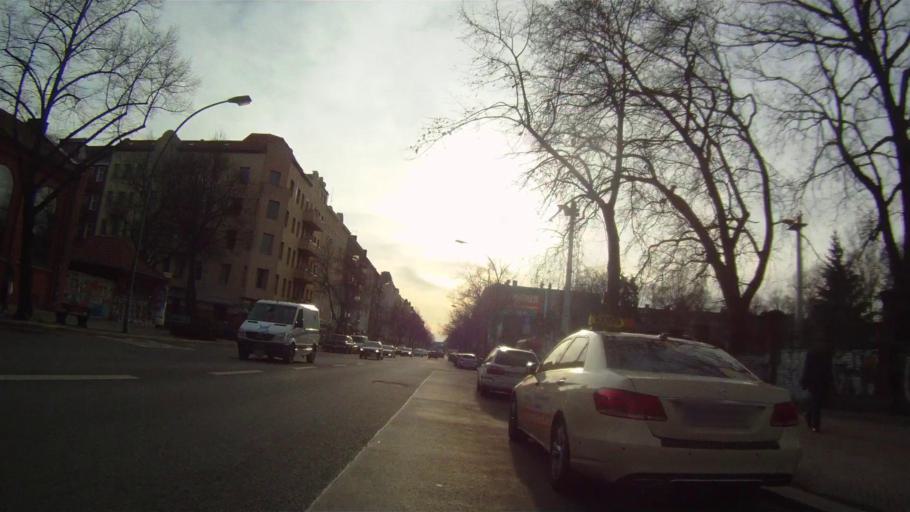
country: DE
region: Berlin
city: Berlin Treptow
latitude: 52.4724
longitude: 13.4287
